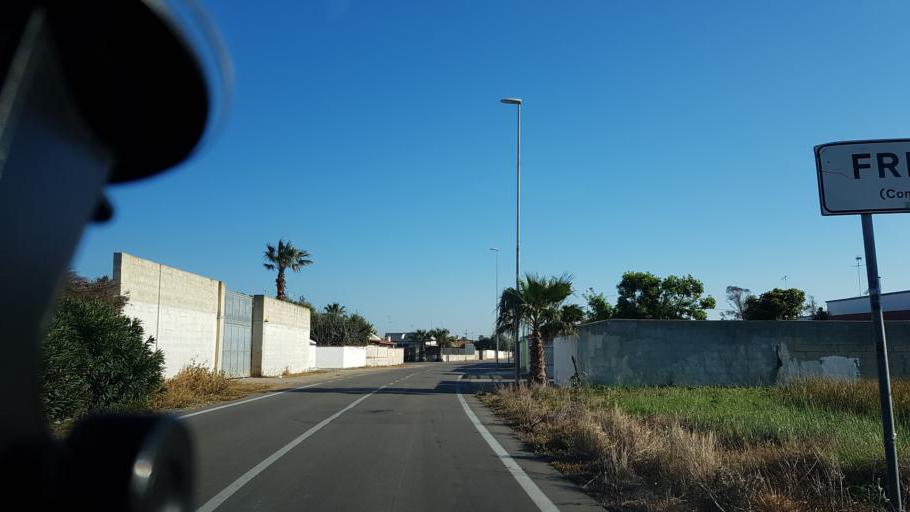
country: IT
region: Apulia
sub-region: Provincia di Lecce
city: Merine
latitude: 40.4315
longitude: 18.2419
